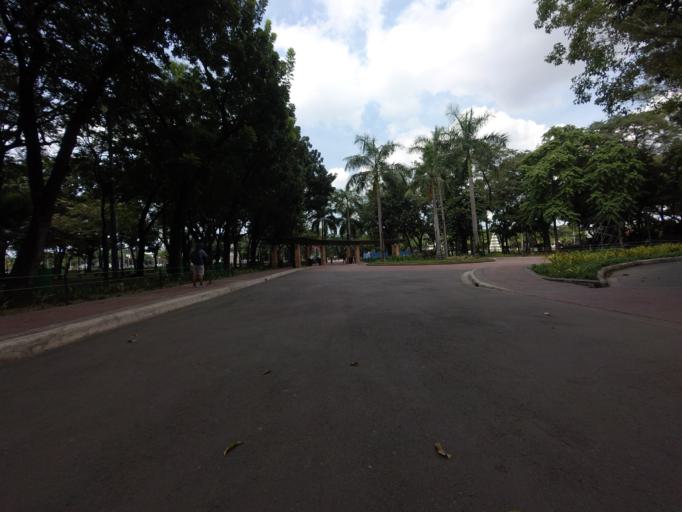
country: PH
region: Metro Manila
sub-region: City of Manila
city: Port Area
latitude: 14.5811
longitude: 120.9779
